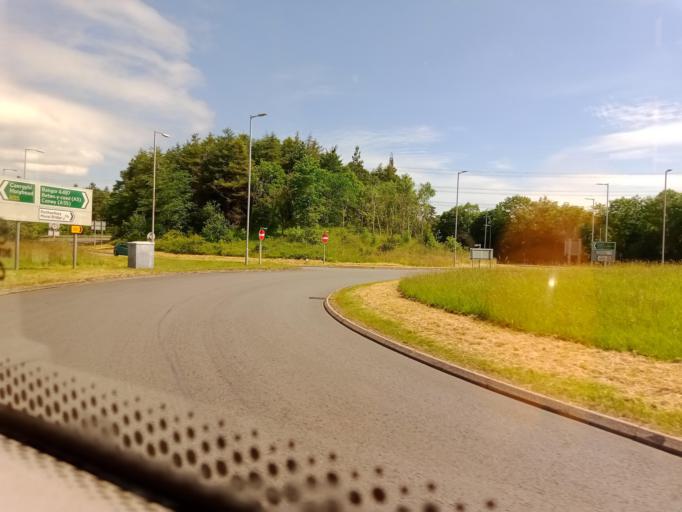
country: GB
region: Wales
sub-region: Anglesey
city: Menai Bridge
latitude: 53.2045
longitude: -4.1774
